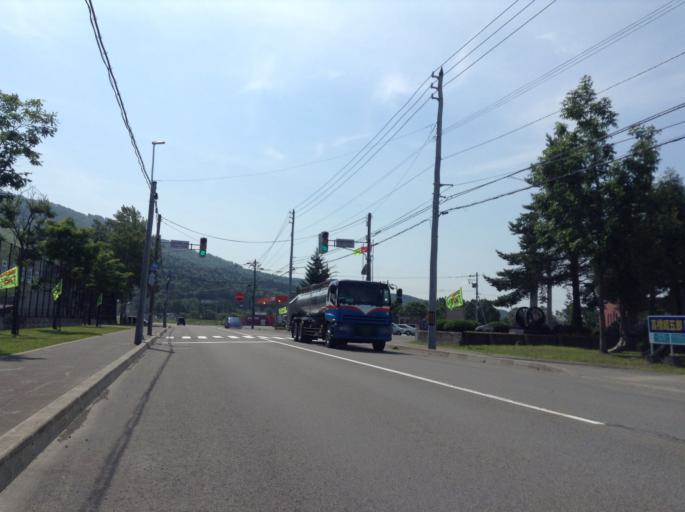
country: JP
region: Hokkaido
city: Nayoro
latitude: 44.7259
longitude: 142.2624
